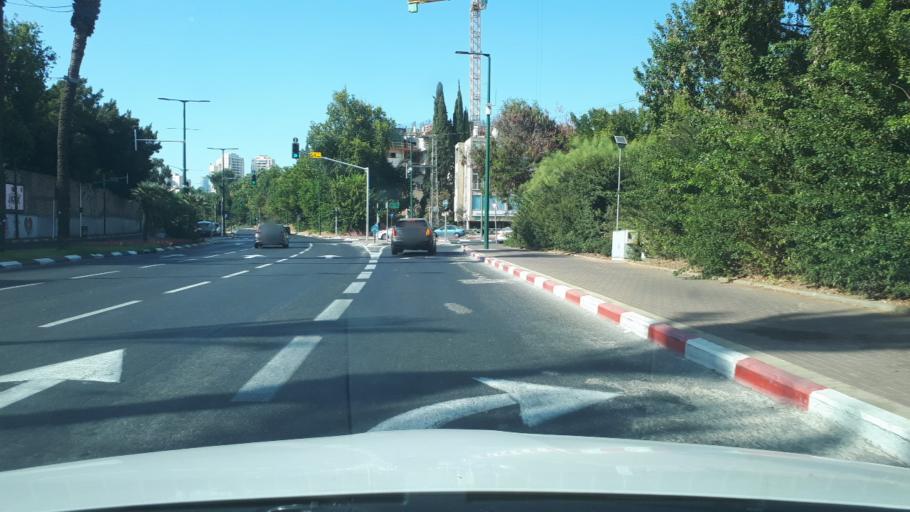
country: IL
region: Tel Aviv
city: Giv`atayim
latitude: 32.0608
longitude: 34.8209
